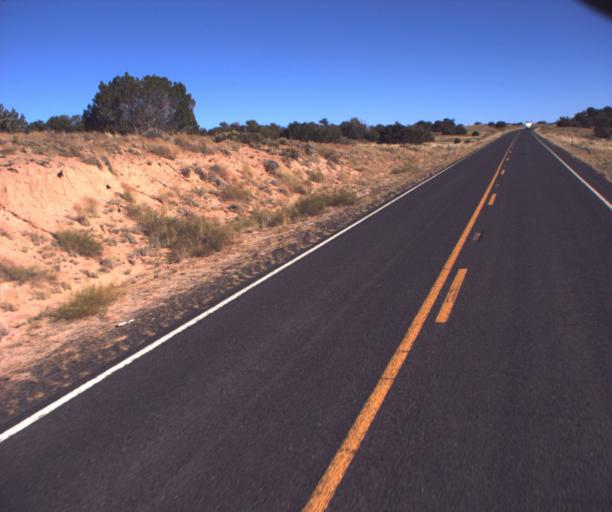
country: US
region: Arizona
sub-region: Apache County
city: Houck
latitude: 35.3633
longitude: -109.4694
